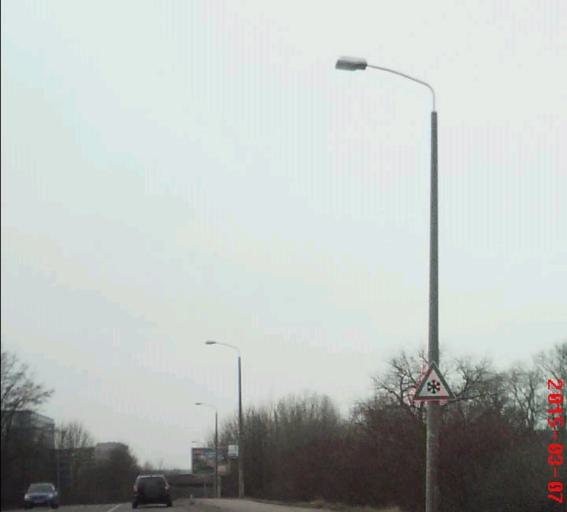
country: DE
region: Thuringia
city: Erfurt
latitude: 51.0106
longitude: 11.0102
